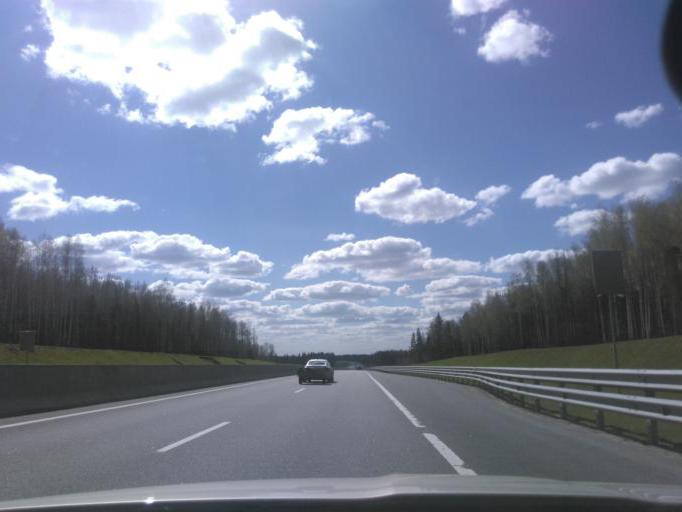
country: RU
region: Moskovskaya
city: Lozhki
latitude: 56.1299
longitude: 37.1081
